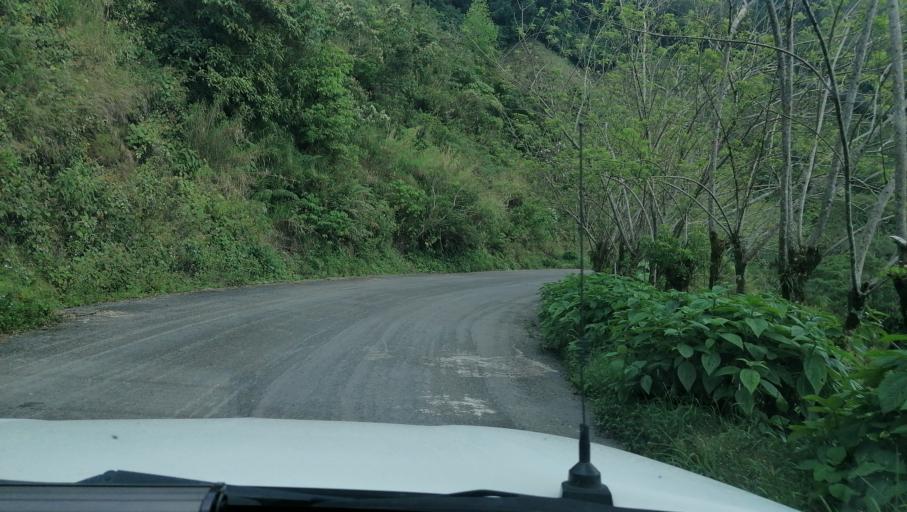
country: MX
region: Chiapas
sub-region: Francisco Leon
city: San Miguel la Sardina
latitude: 17.2453
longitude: -93.2917
